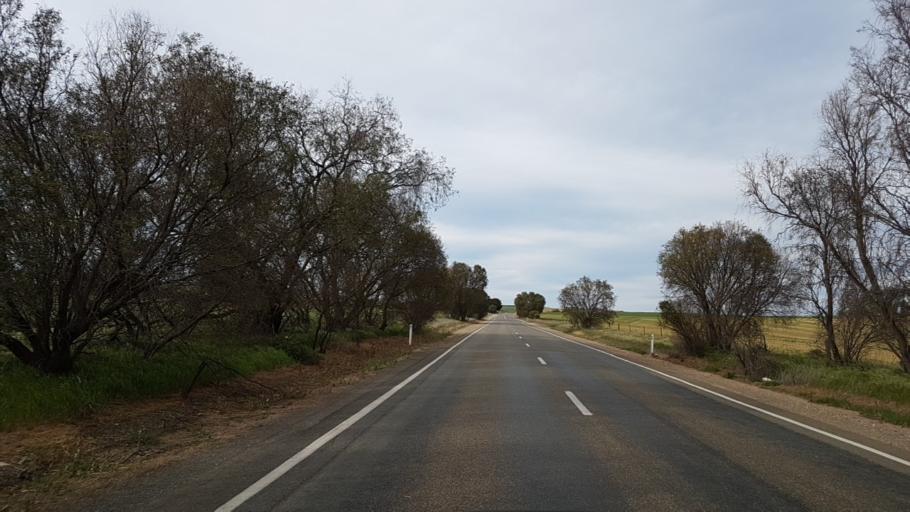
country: AU
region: South Australia
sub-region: Northern Areas
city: Jamestown
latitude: -33.2190
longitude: 138.4135
